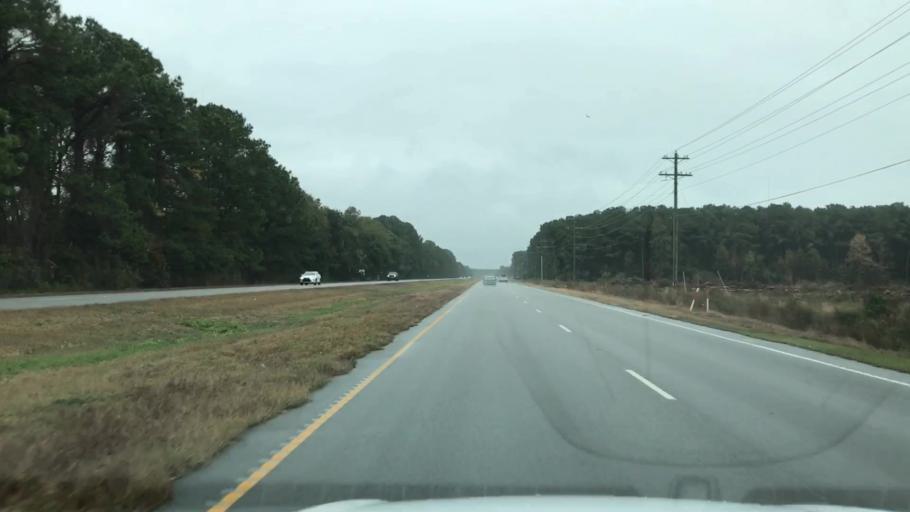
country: US
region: South Carolina
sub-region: Charleston County
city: Isle of Palms
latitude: 32.9060
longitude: -79.7265
